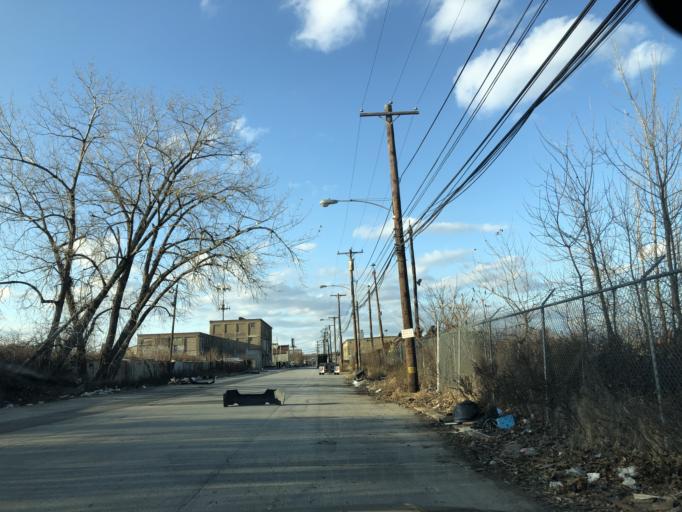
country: US
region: New Jersey
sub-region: Camden County
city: Pennsauken
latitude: 39.9821
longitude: -75.0904
